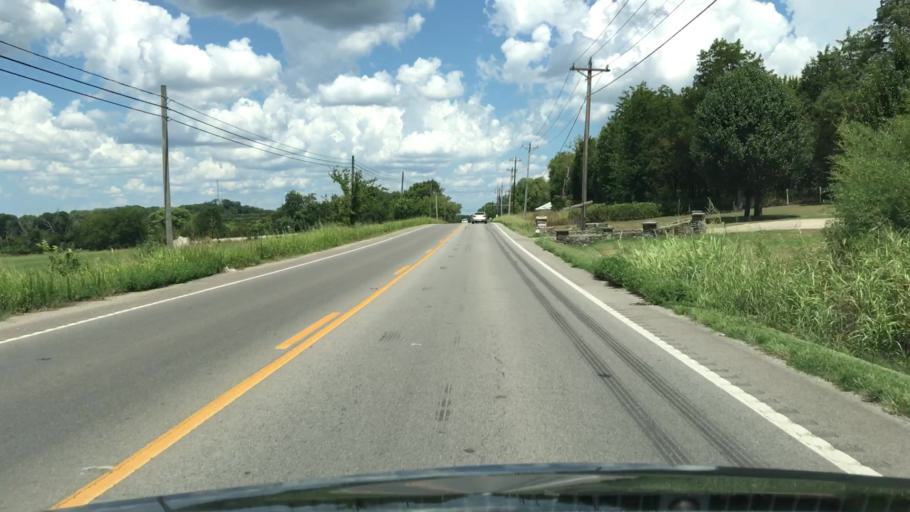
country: US
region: Tennessee
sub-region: Williamson County
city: Nolensville
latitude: 35.9350
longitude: -86.6600
